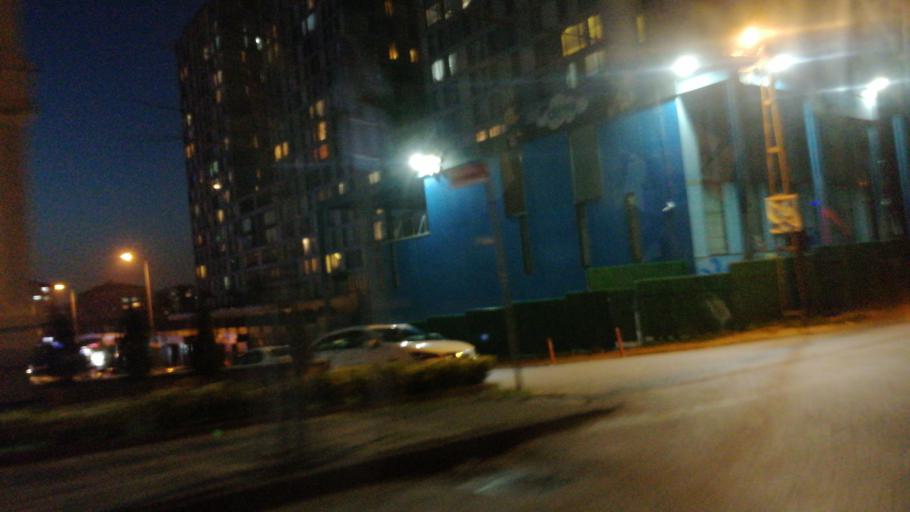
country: TR
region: Istanbul
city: Umraniye
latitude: 40.9985
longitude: 29.1425
